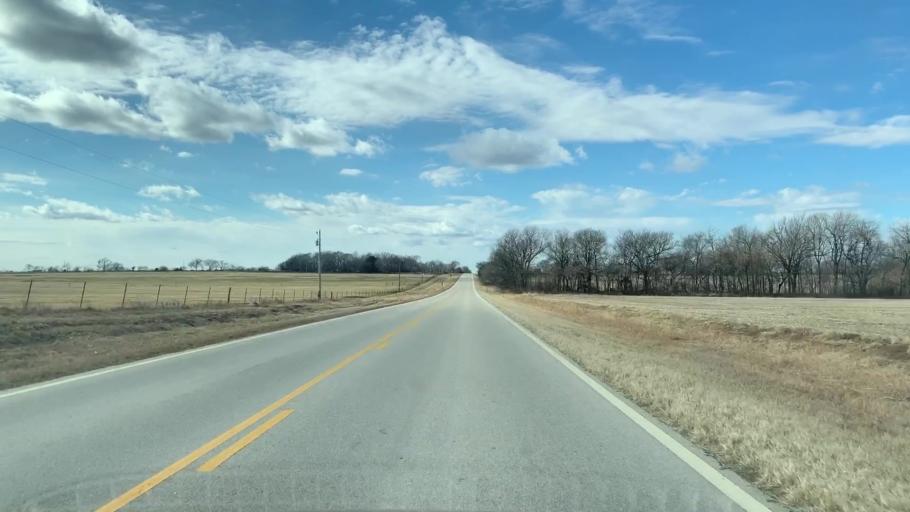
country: US
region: Kansas
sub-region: Neosho County
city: Chanute
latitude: 37.5288
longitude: -95.4365
